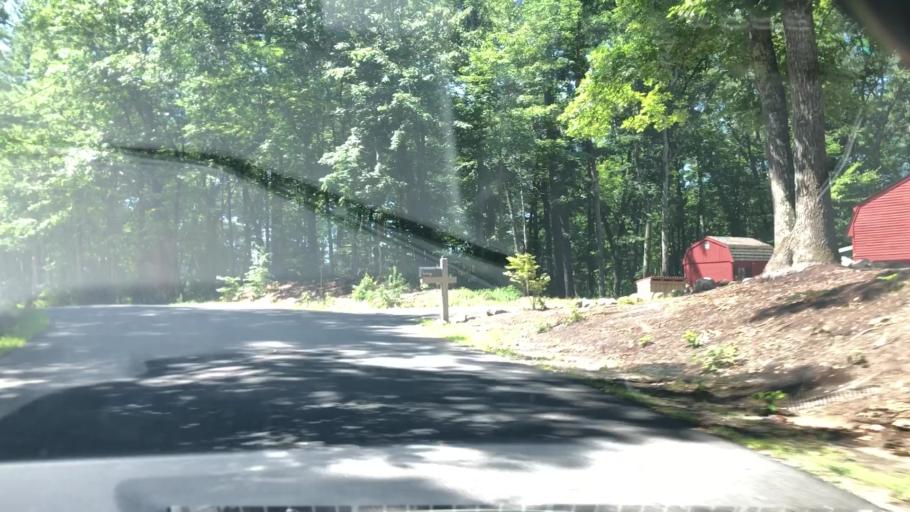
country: US
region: New Hampshire
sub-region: Hillsborough County
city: Milford
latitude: 42.8382
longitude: -71.5791
